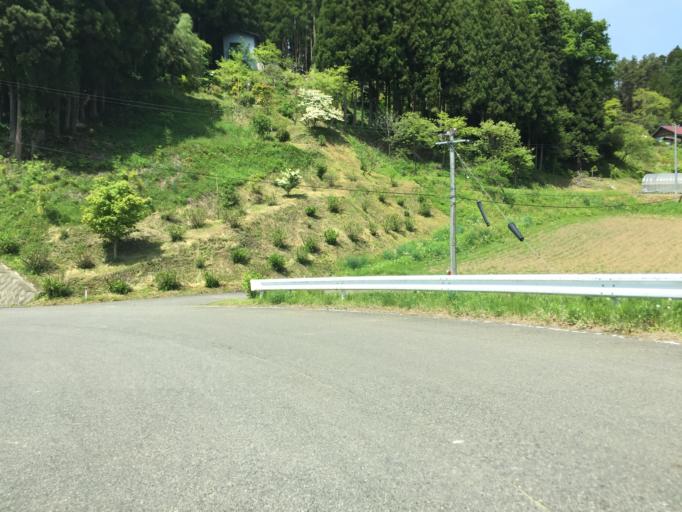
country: JP
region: Fukushima
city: Ishikawa
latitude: 37.1691
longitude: 140.5063
